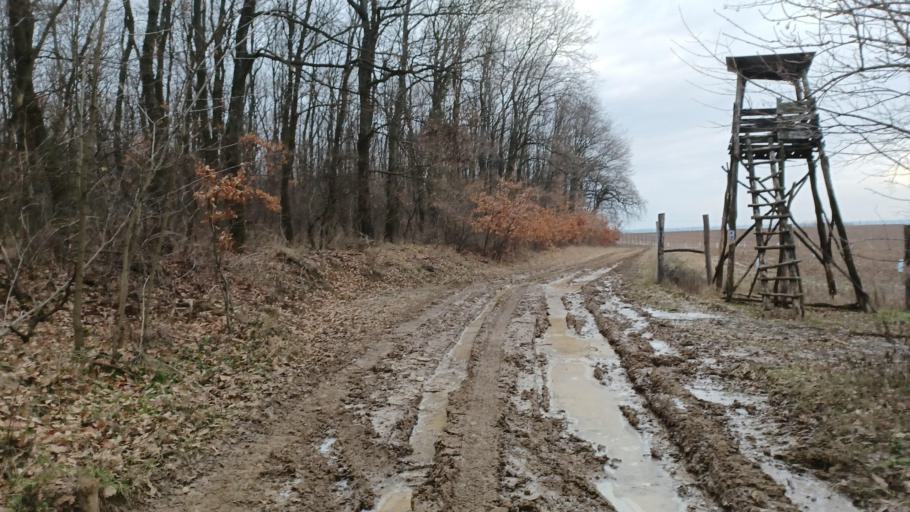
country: HU
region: Tolna
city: Szentgalpuszta
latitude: 46.2964
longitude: 18.6276
